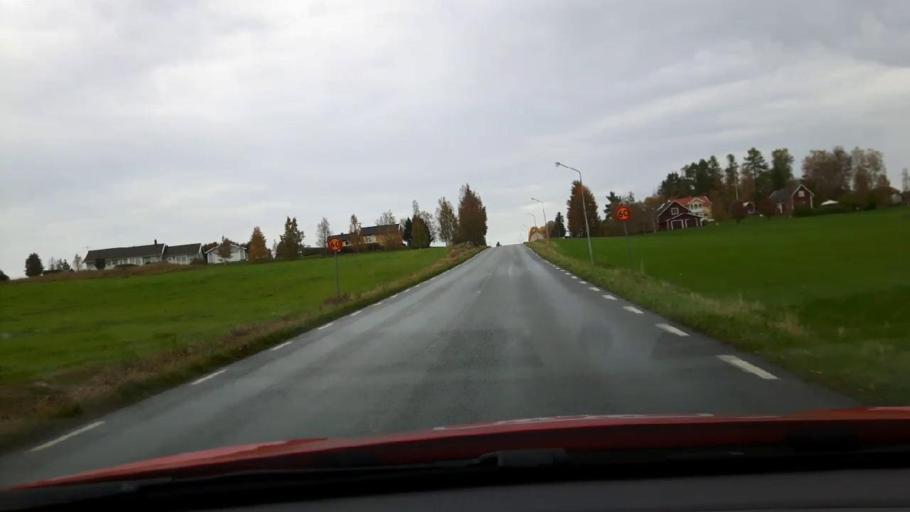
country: SE
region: Jaemtland
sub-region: Bergs Kommun
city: Hoverberg
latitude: 63.0064
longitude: 14.3400
